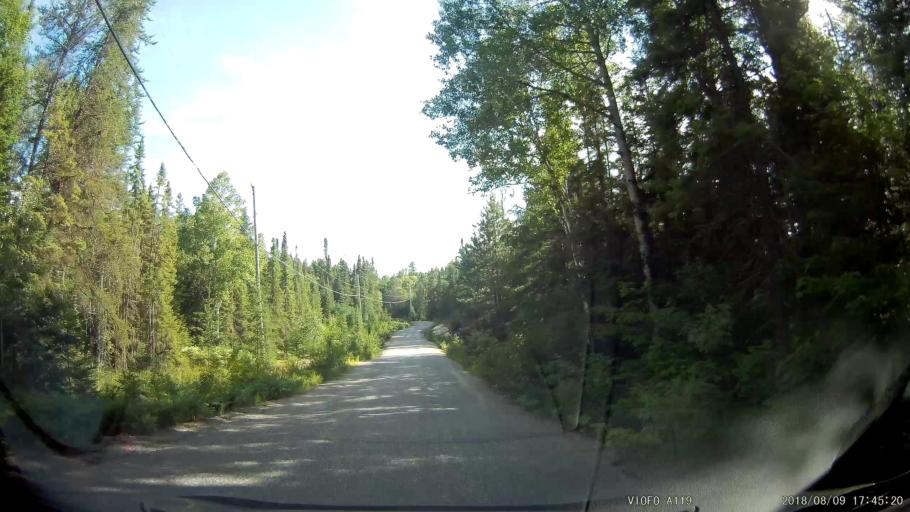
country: CA
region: Ontario
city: Rayside-Balfour
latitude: 46.6010
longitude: -81.5340
